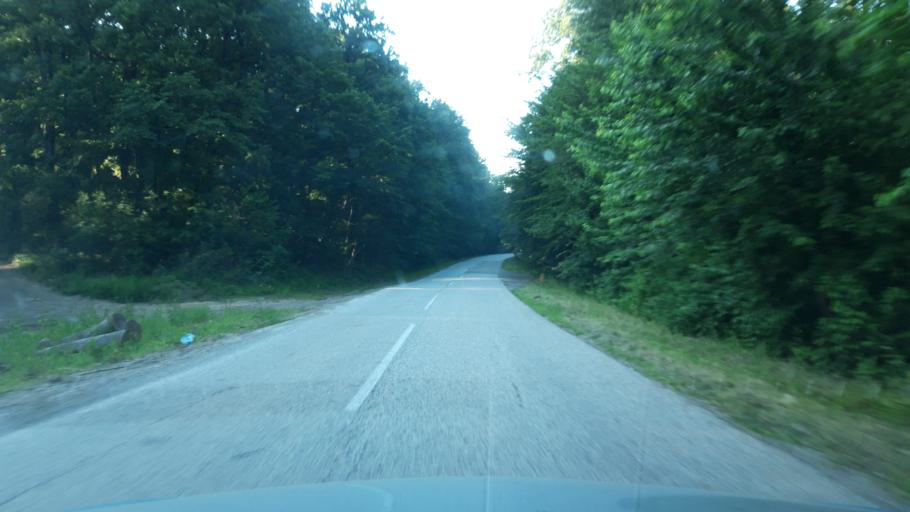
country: RS
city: Glozan
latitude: 45.1556
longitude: 19.5865
